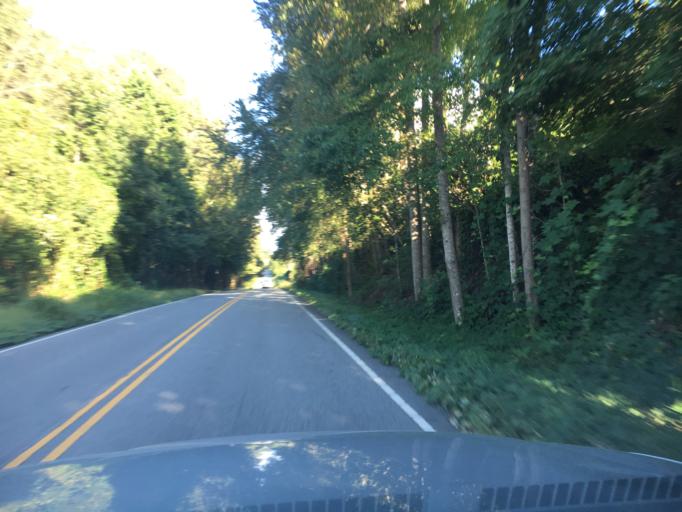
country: US
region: South Carolina
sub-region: Spartanburg County
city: Woodruff
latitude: 34.7912
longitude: -82.1251
